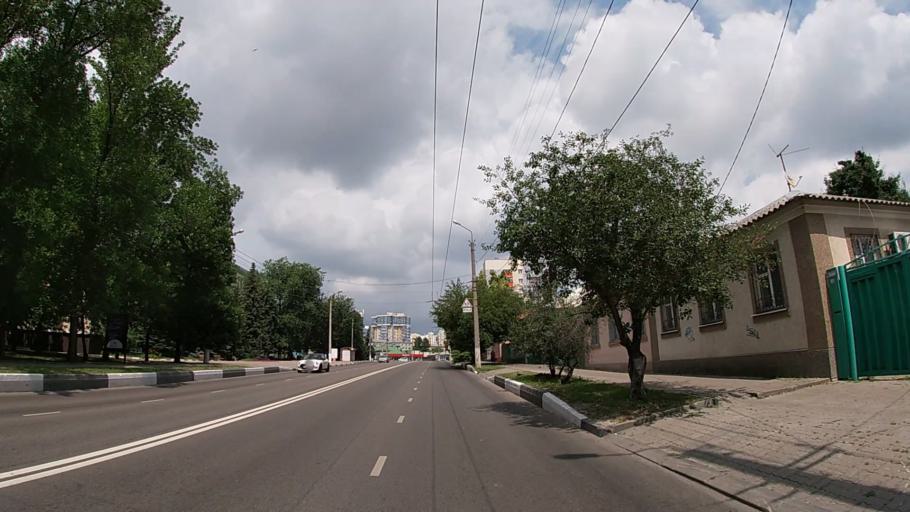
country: RU
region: Belgorod
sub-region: Belgorodskiy Rayon
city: Belgorod
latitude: 50.6080
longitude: 36.5916
